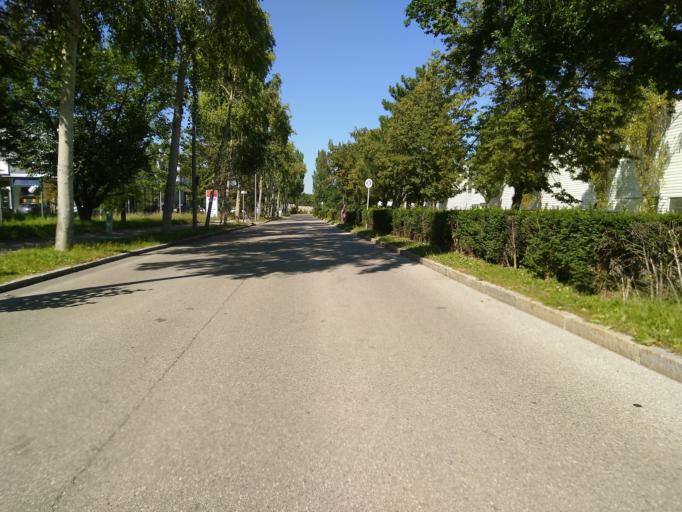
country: DE
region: Bavaria
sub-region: Upper Bavaria
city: Bogenhausen
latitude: 48.1943
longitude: 11.5964
